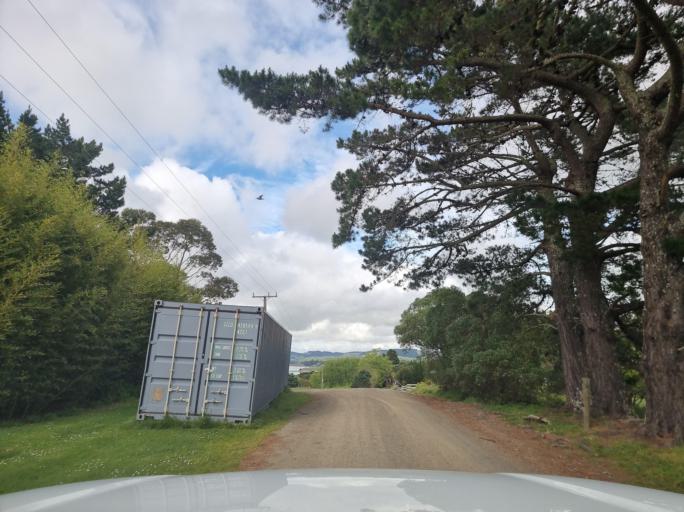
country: NZ
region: Northland
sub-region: Whangarei
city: Ruakaka
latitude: -36.1312
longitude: 174.2083
